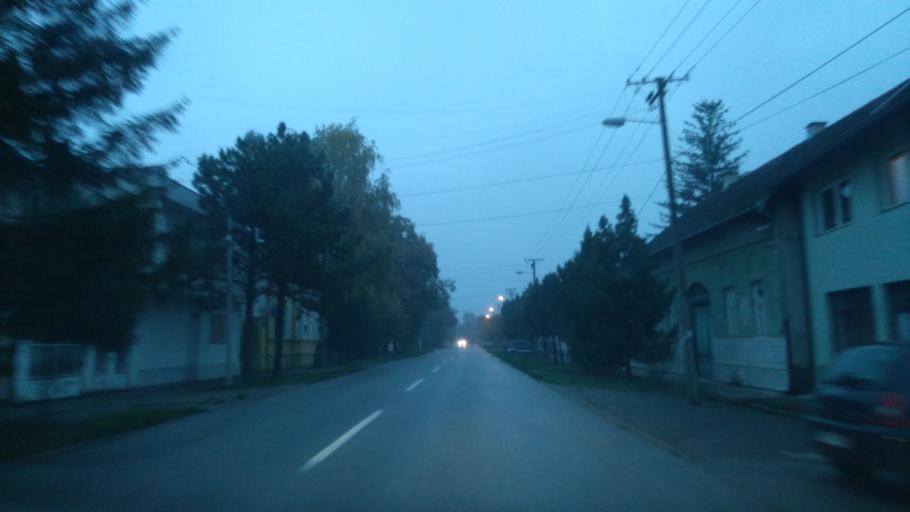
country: RS
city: Backo Petrovo Selo
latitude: 45.7064
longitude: 20.0870
